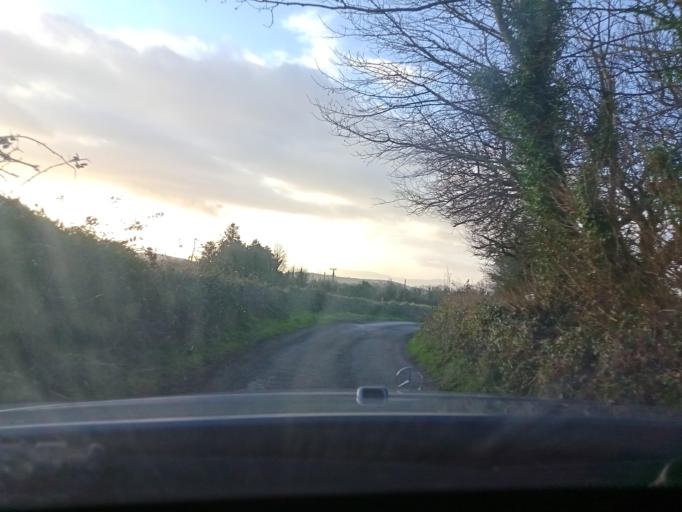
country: IE
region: Leinster
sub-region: Kilkenny
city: Callan
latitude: 52.4579
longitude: -7.4235
